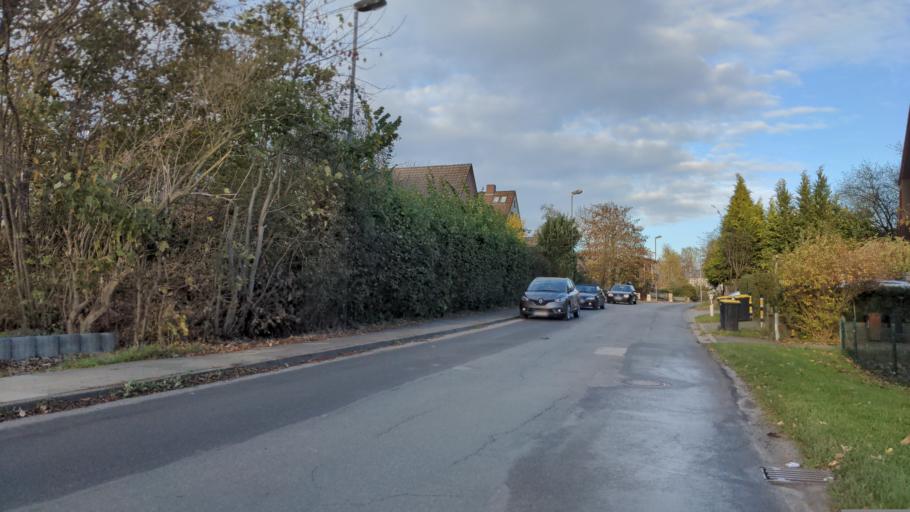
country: DE
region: Schleswig-Holstein
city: Reinfeld
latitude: 53.8378
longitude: 10.4933
